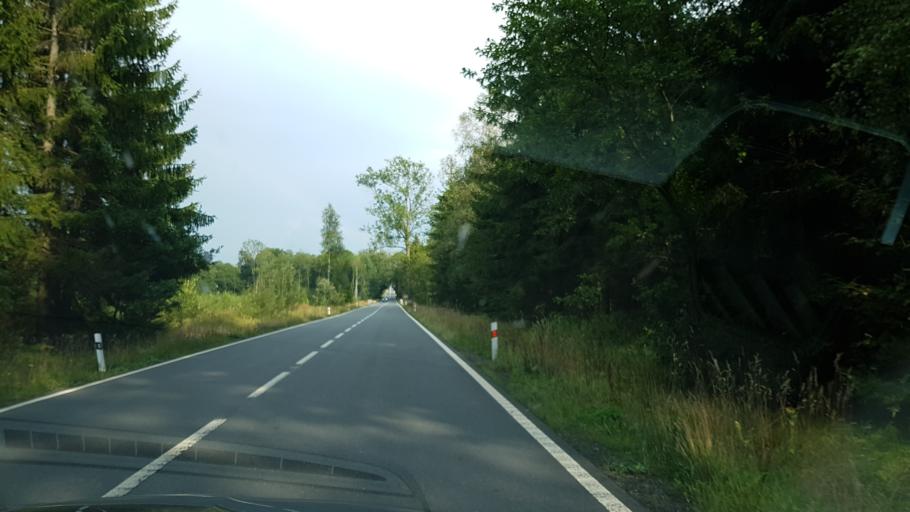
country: CZ
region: Pardubicky
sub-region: Okres Usti nad Orlici
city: Kraliky
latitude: 50.0876
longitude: 16.7277
